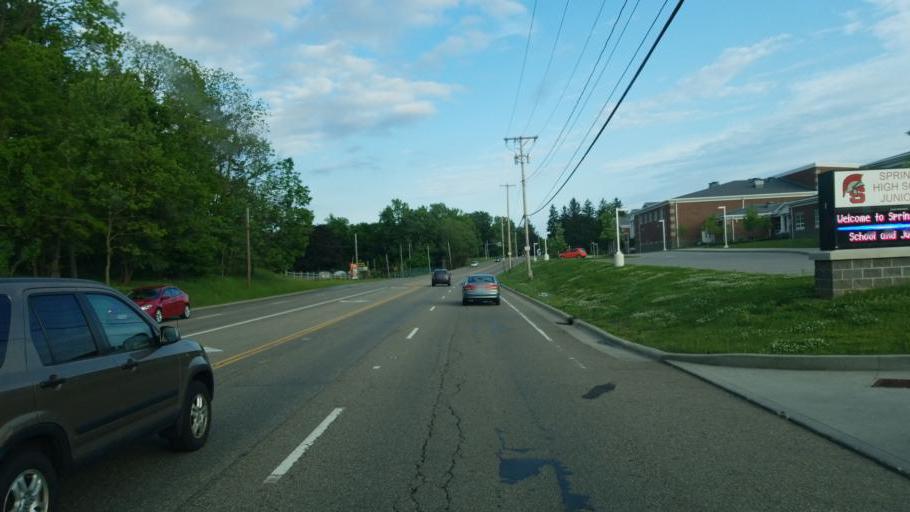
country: US
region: Ohio
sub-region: Summit County
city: Lakemore
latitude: 41.0186
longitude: -81.4150
